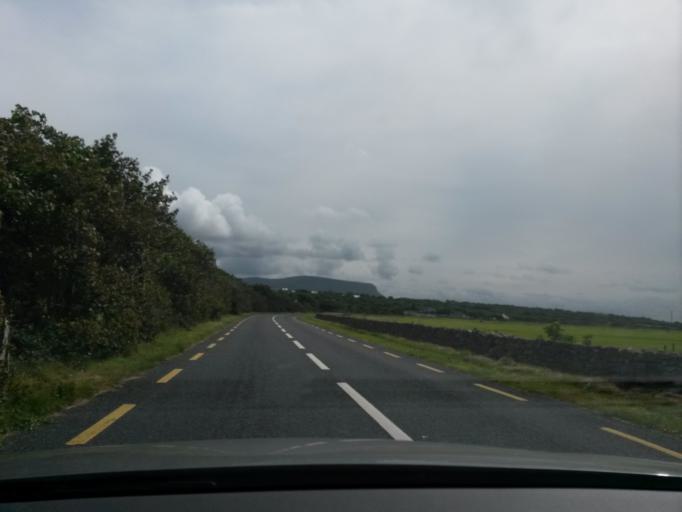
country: IE
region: Connaught
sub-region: Sligo
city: Sligo
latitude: 54.4378
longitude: -8.4554
